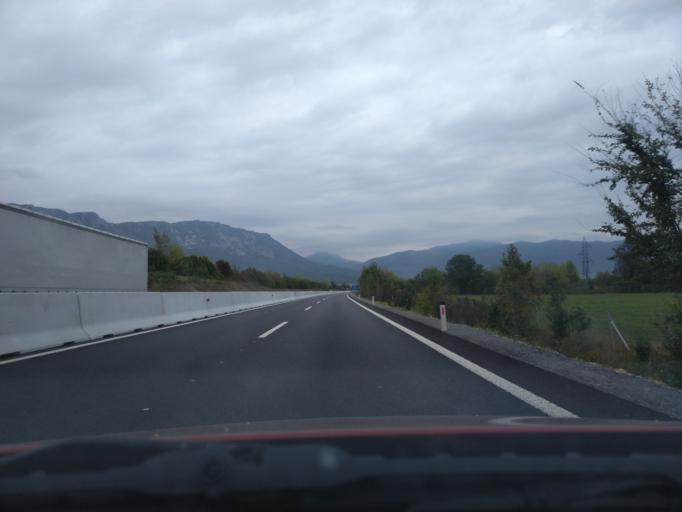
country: SI
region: Ajdovscina
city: Lokavec
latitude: 45.8846
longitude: 13.8780
